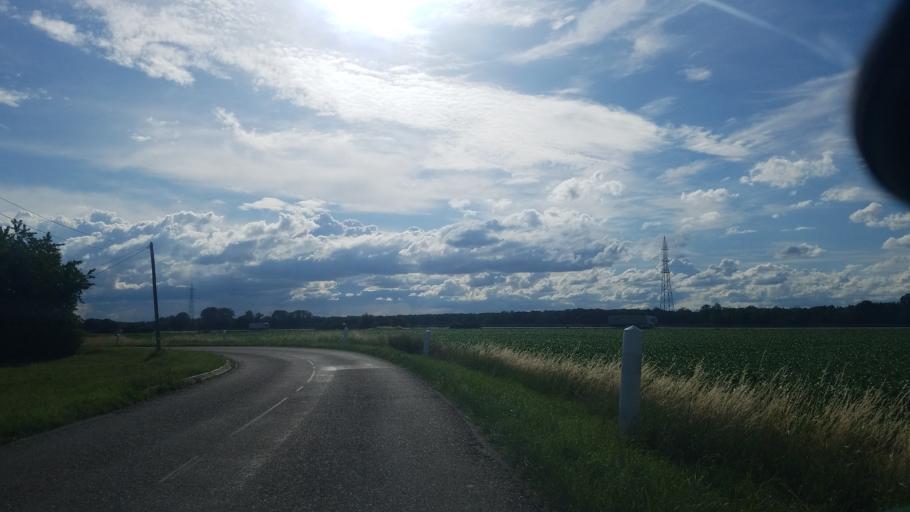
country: FR
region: Alsace
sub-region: Departement du Bas-Rhin
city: Drusenheim
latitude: 48.7769
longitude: 7.9544
